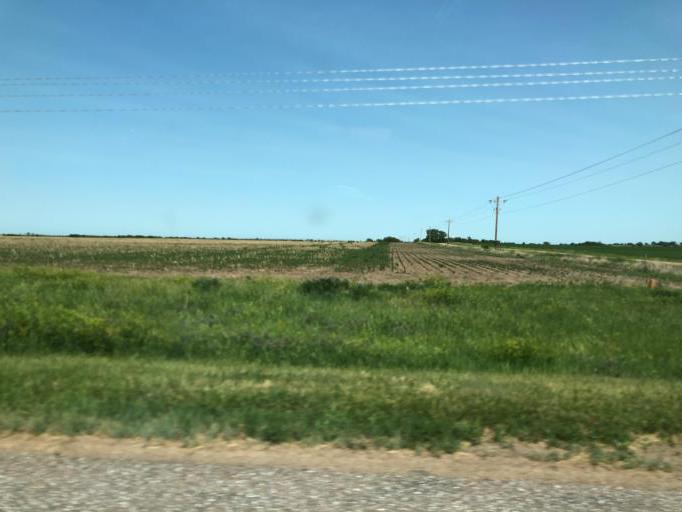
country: US
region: Nebraska
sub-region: Fillmore County
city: Geneva
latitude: 40.3938
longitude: -97.5772
